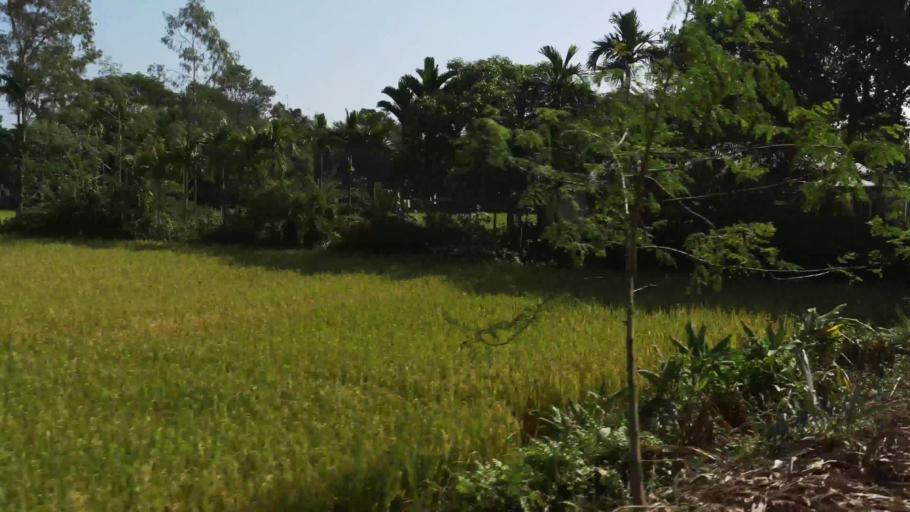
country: BD
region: Dhaka
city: Gafargaon
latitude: 24.5436
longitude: 90.5085
